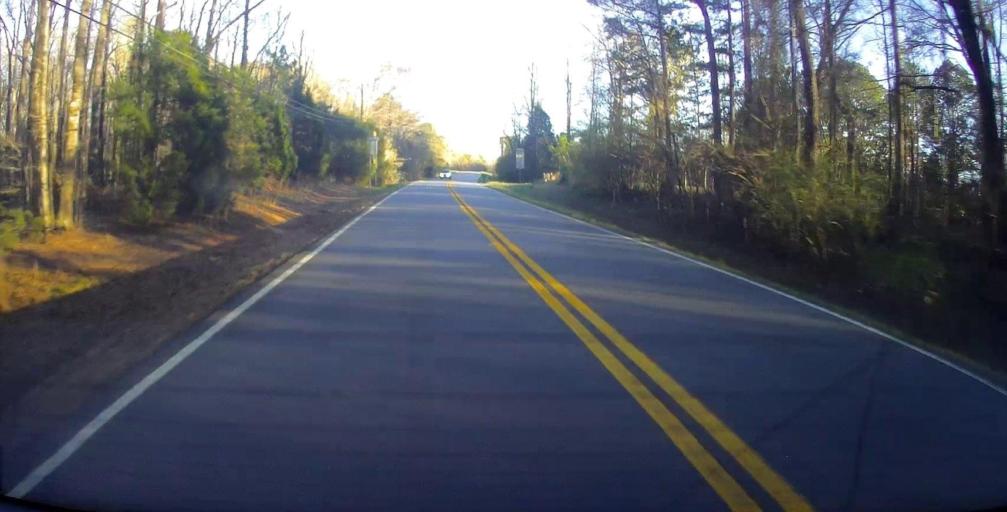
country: US
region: Georgia
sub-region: Harris County
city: Hamilton
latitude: 32.6302
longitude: -84.8243
